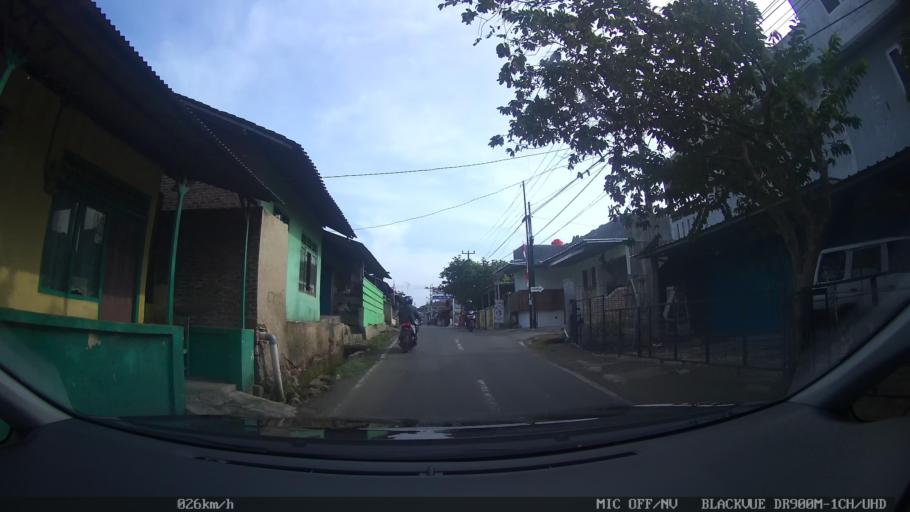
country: ID
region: Lampung
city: Kedaton
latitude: -5.3928
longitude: 105.2662
